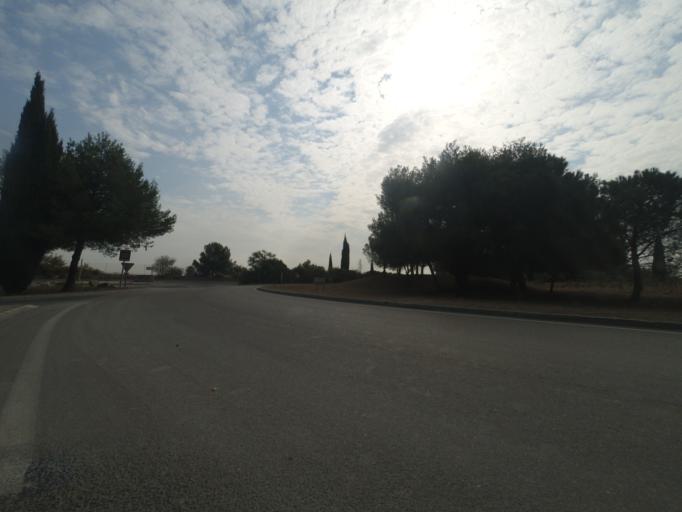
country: FR
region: Languedoc-Roussillon
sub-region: Departement de l'Herault
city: Lunel
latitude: 43.7043
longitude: 4.1220
